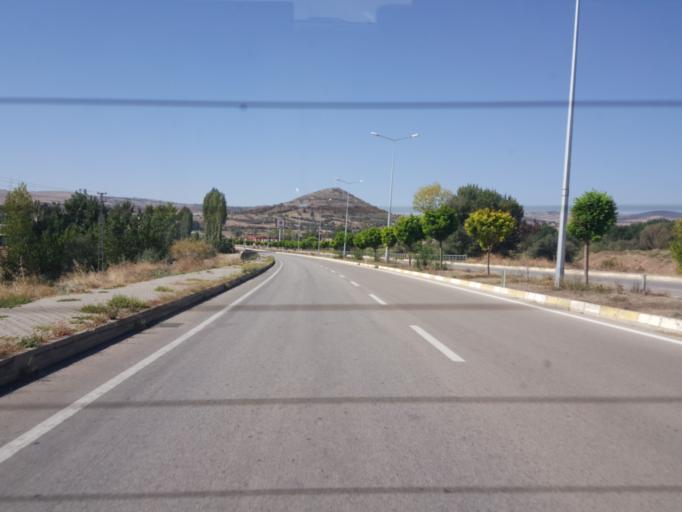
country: TR
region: Tokat
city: Zile
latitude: 40.2911
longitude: 35.8702
